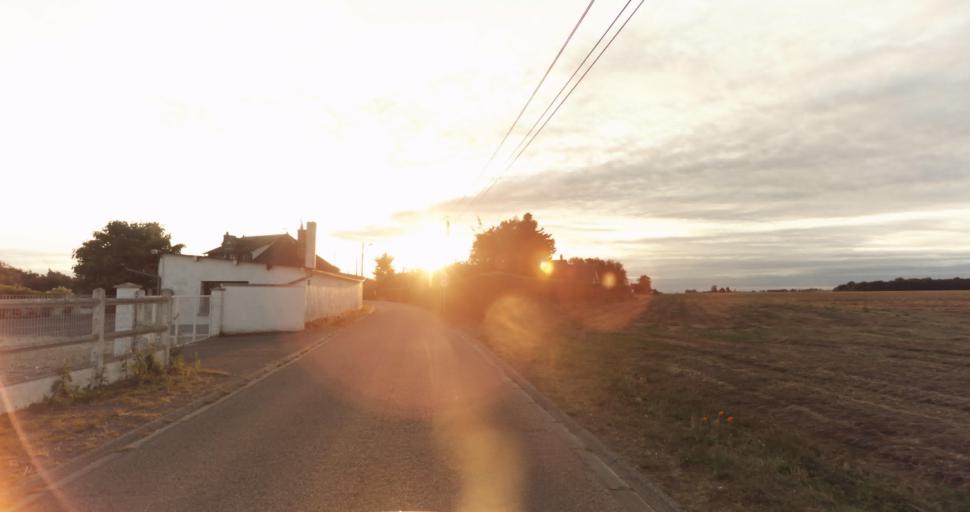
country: FR
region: Haute-Normandie
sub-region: Departement de l'Eure
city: La Madeleine-de-Nonancourt
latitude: 48.8754
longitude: 1.2093
